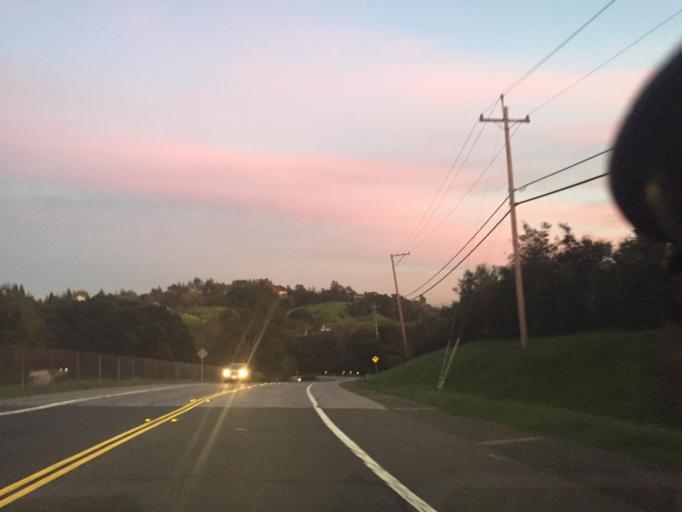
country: US
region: California
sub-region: Santa Clara County
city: Los Altos Hills
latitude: 37.3875
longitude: -122.1560
